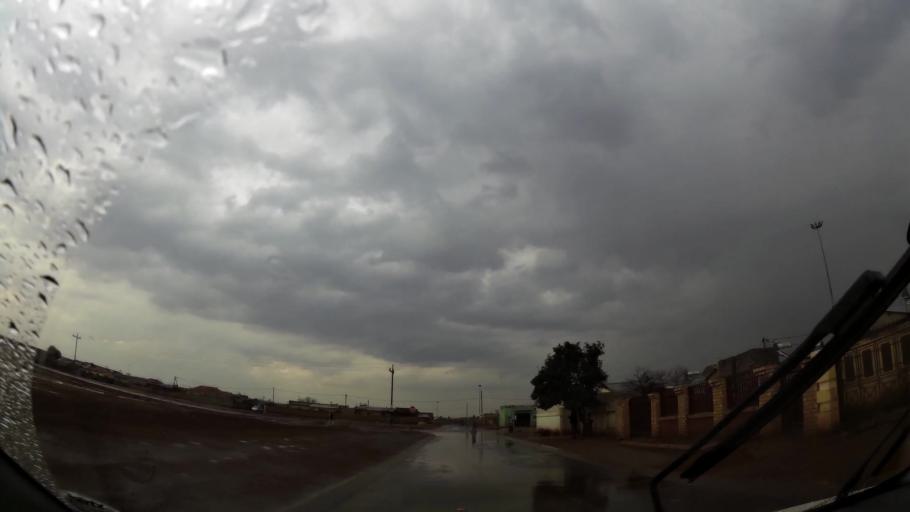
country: ZA
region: Gauteng
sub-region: Ekurhuleni Metropolitan Municipality
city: Germiston
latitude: -26.3731
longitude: 28.1505
